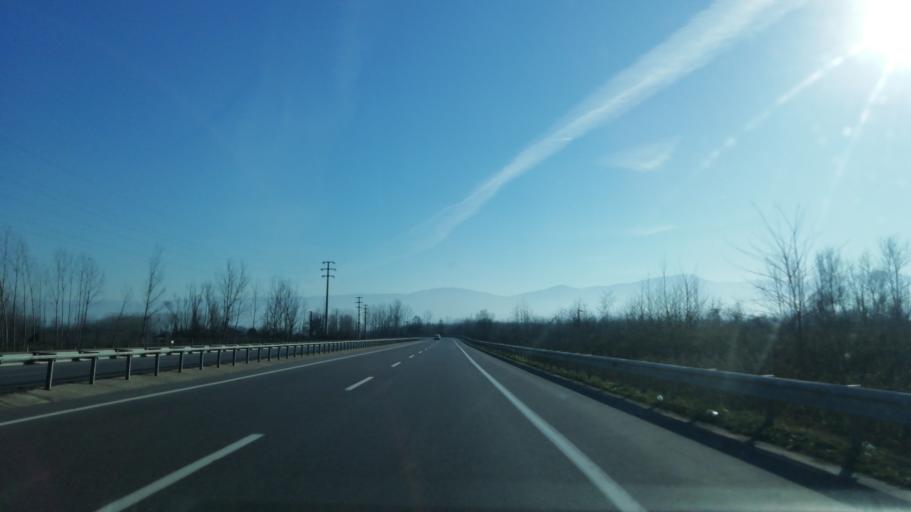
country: TR
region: Sakarya
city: Akyazi
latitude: 40.7017
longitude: 30.5673
